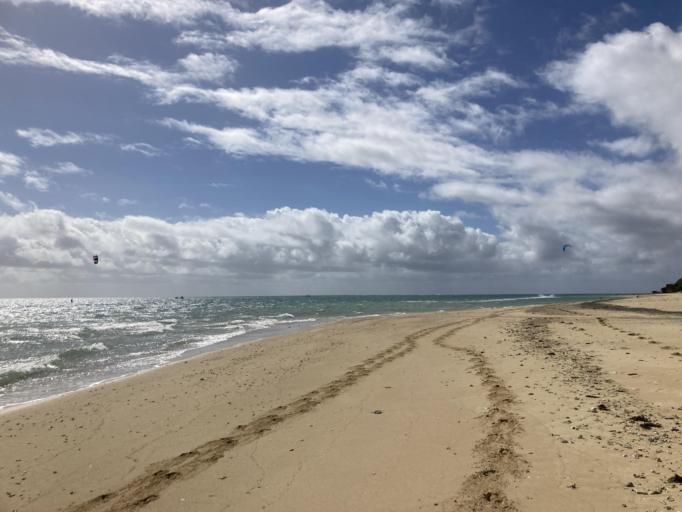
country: JP
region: Okinawa
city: Tomigusuku
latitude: 26.1385
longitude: 127.7959
